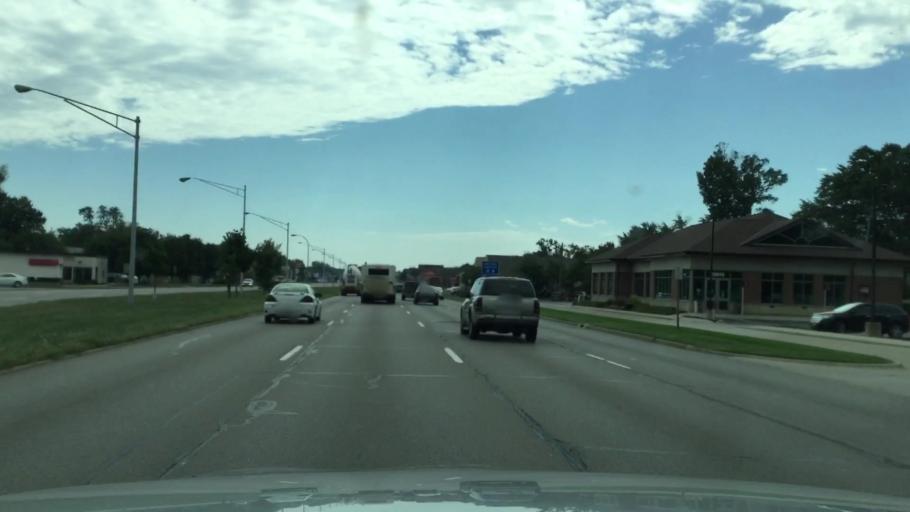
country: US
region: Michigan
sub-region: Oakland County
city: Berkley
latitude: 42.5008
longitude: -83.1699
